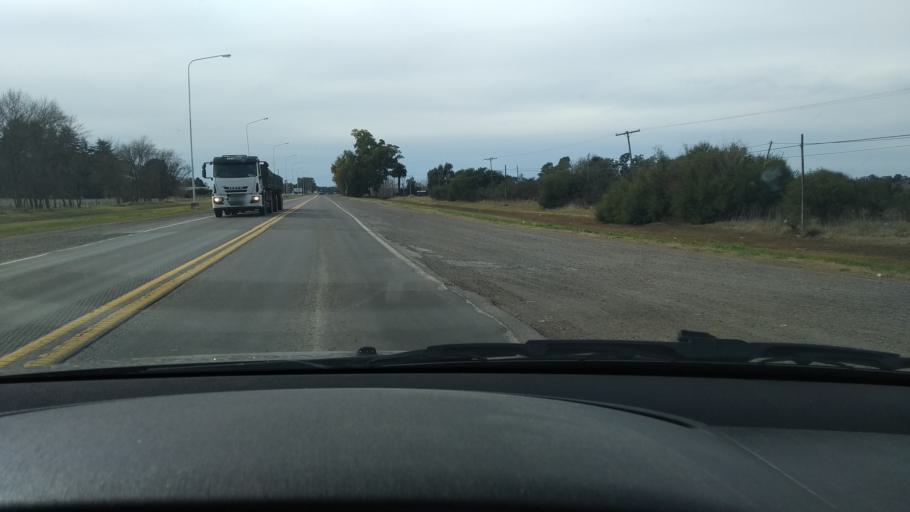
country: AR
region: Buenos Aires
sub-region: Partido de Azul
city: Azul
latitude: -36.7823
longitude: -59.8289
